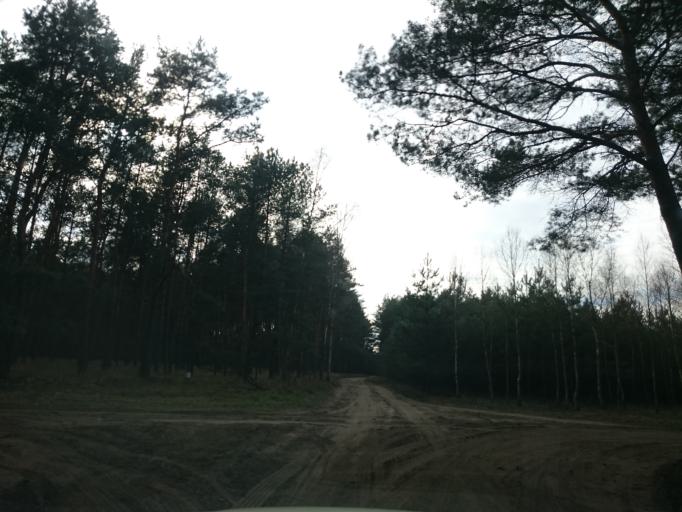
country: PL
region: Kujawsko-Pomorskie
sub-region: Powiat golubsko-dobrzynski
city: Ciechocin
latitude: 53.0497
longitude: 18.8643
